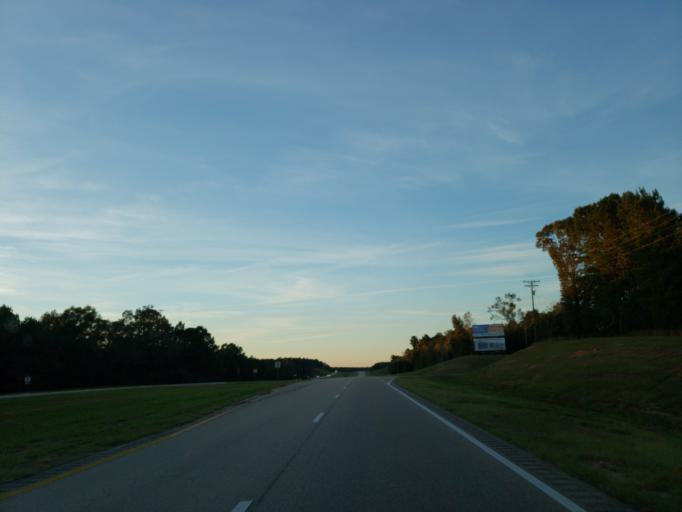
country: US
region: Mississippi
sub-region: Wayne County
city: Belmont
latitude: 31.4735
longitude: -88.4787
